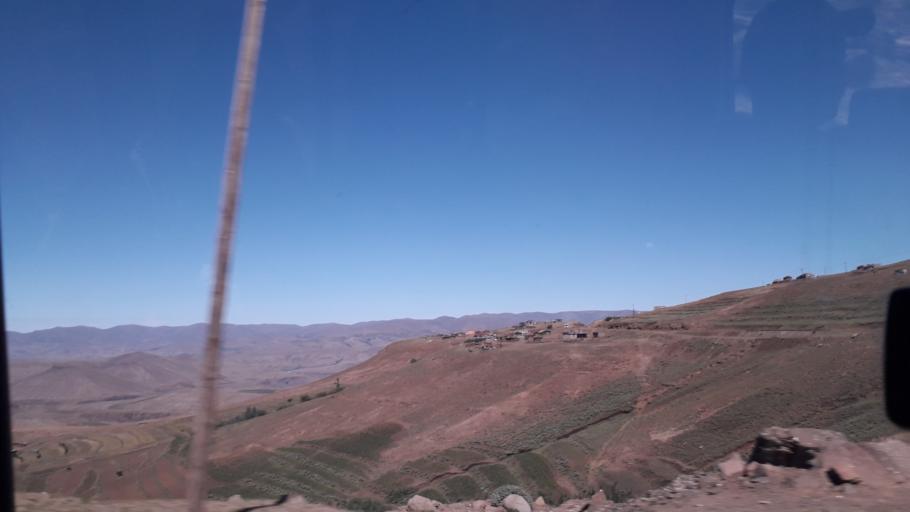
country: LS
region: Mokhotlong
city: Mokhotlong
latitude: -29.2794
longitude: 28.9427
